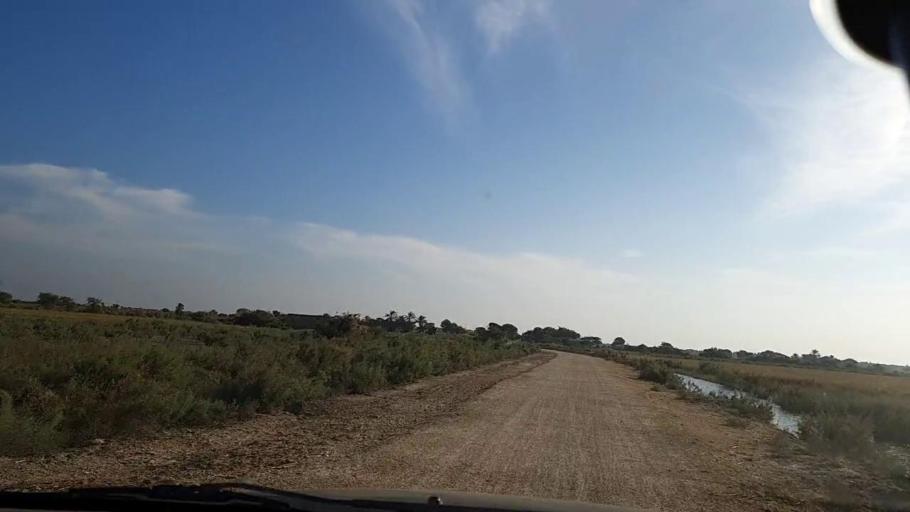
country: PK
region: Sindh
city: Mirpur Batoro
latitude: 24.6555
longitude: 68.3092
